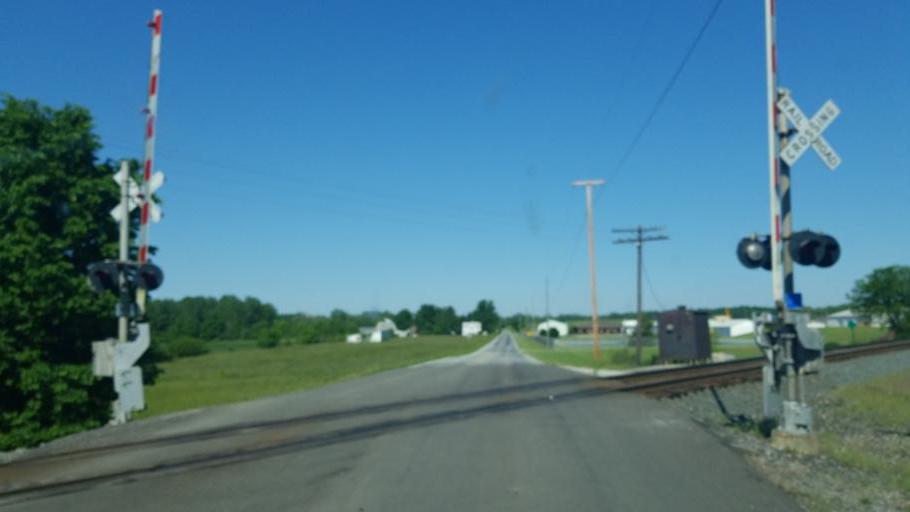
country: US
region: Ohio
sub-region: Hardin County
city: Kenton
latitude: 40.6477
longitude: -83.6265
